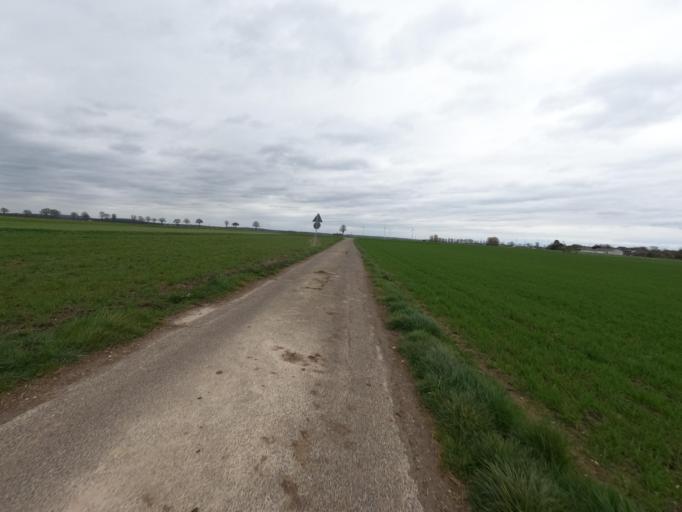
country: DE
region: North Rhine-Westphalia
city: Huckelhoven
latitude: 50.9972
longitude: 6.1982
